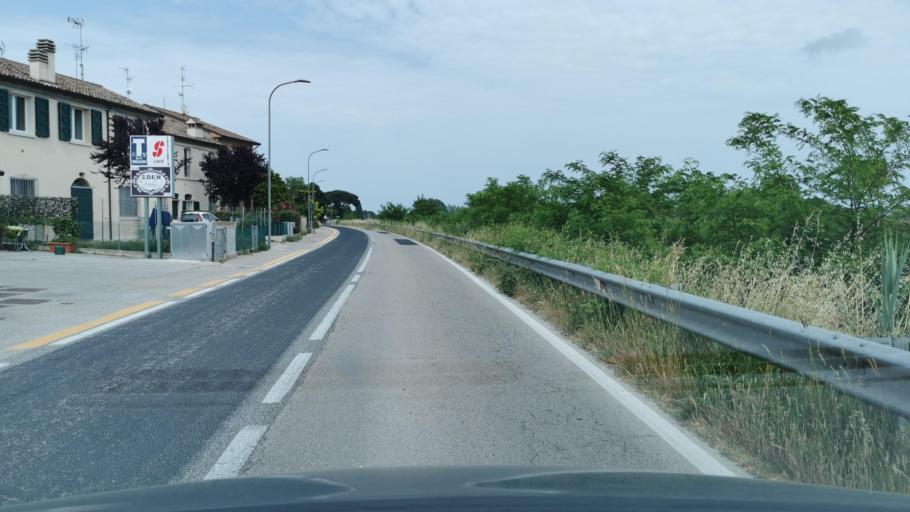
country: IT
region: Emilia-Romagna
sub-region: Provincia di Ravenna
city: Marina Romea
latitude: 44.5527
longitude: 12.2250
